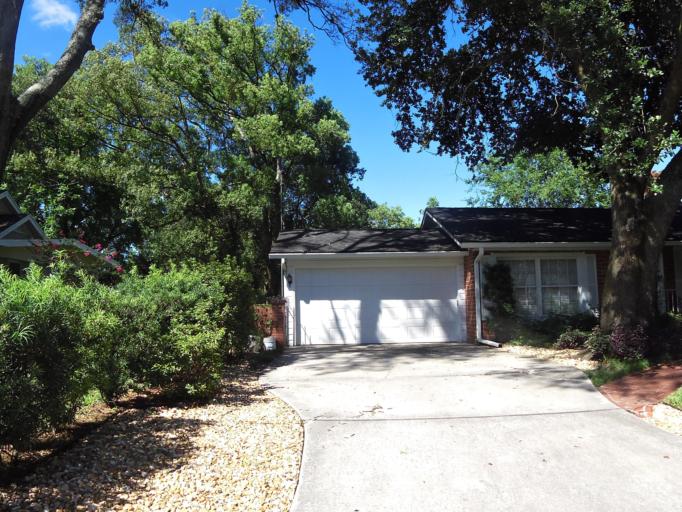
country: US
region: Florida
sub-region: Duval County
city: Jacksonville
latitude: 30.2989
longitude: -81.7156
